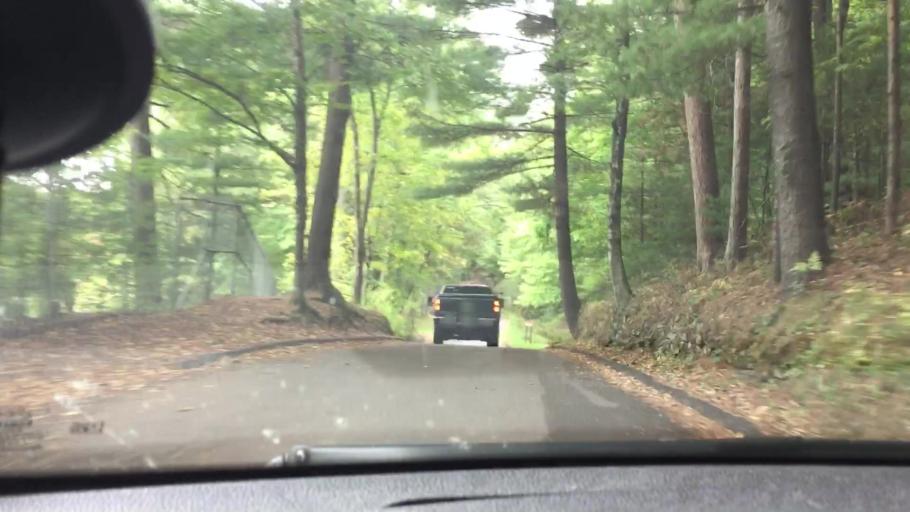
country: US
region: Wisconsin
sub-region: Chippewa County
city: Chippewa Falls
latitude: 44.9496
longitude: -91.4005
